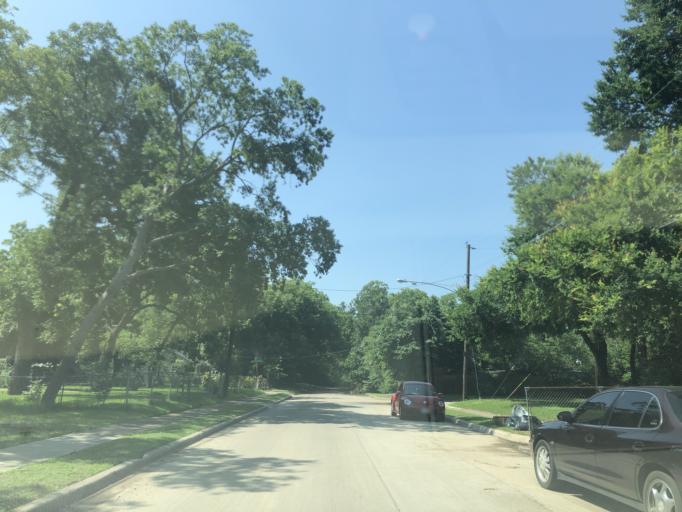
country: US
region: Texas
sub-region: Dallas County
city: Cockrell Hill
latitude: 32.7904
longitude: -96.8720
